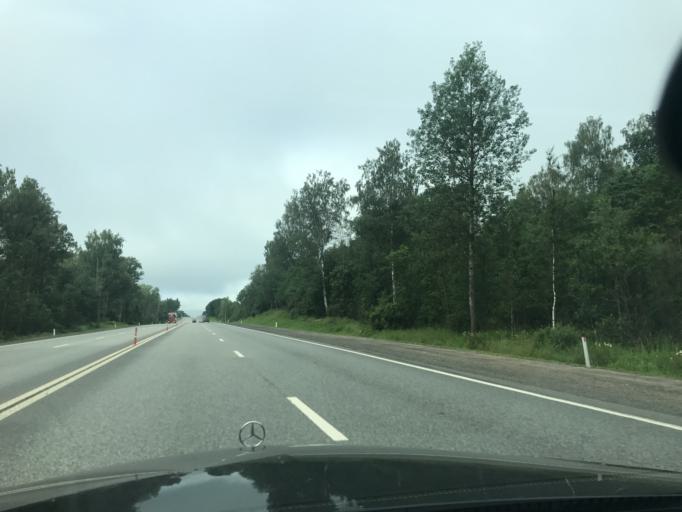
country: RU
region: Smolensk
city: Vyaz'ma
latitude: 55.2878
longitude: 34.4521
